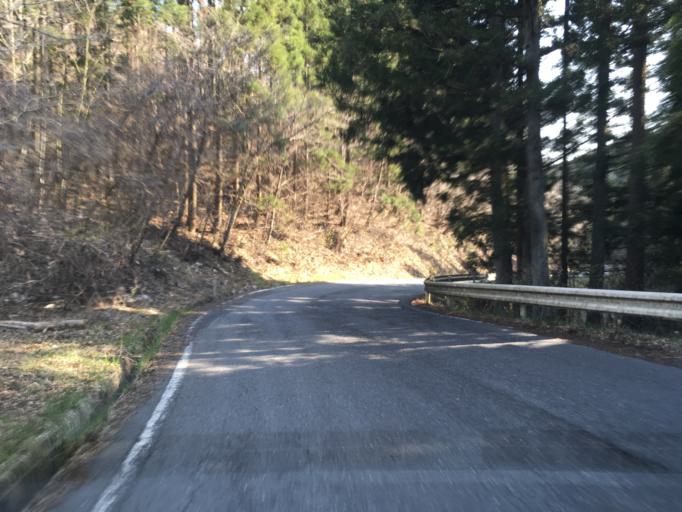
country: JP
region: Iwate
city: Ichinoseki
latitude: 38.8188
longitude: 141.3148
